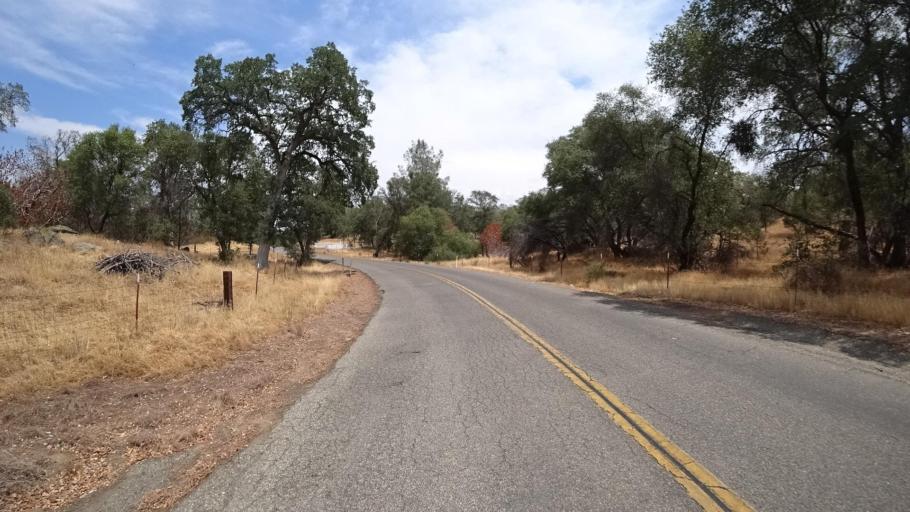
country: US
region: California
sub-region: Mariposa County
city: Mariposa
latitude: 37.4330
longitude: -119.8581
